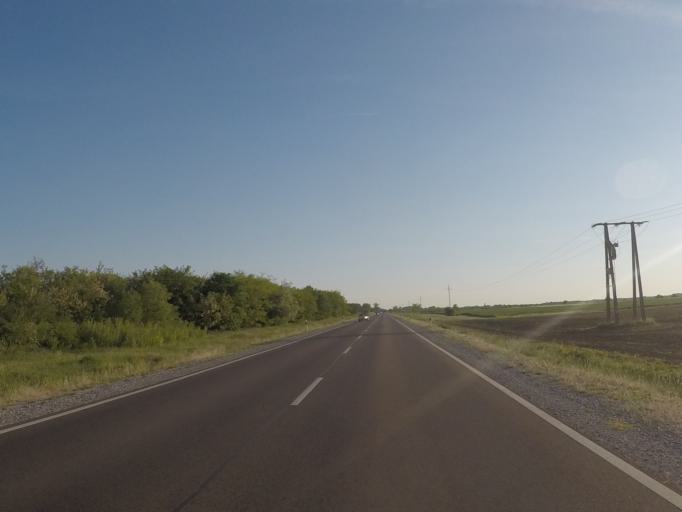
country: HU
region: Heves
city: Erdotelek
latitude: 47.6736
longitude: 20.3696
